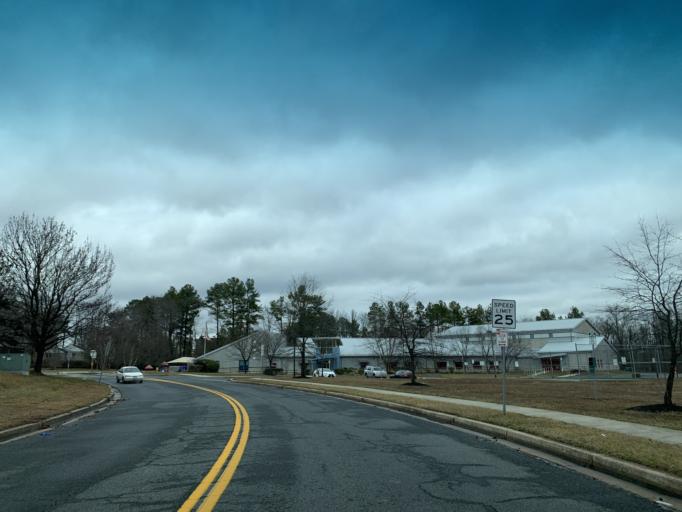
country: US
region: Maryland
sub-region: Harford County
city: Edgewood
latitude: 39.4327
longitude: -76.3099
